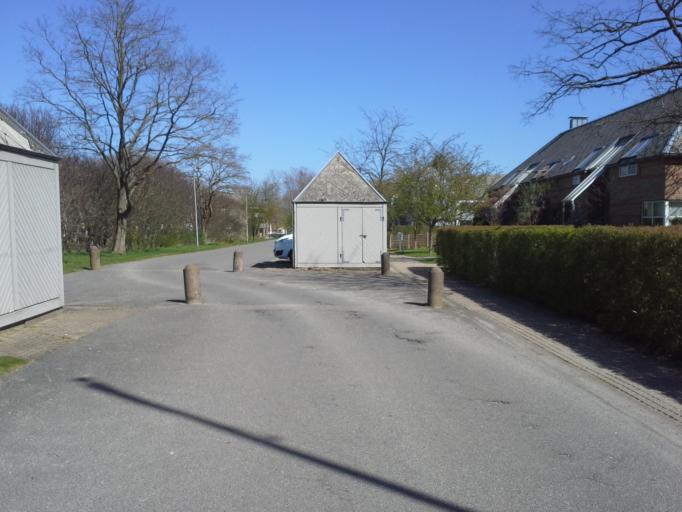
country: DK
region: South Denmark
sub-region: Odense Kommune
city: Neder Holluf
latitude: 55.3796
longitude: 10.4505
